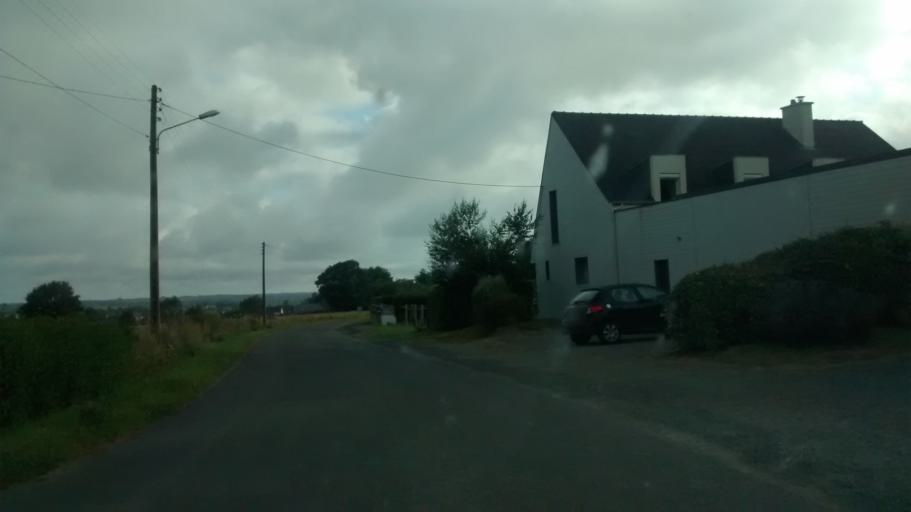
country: FR
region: Brittany
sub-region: Departement d'Ille-et-Vilaine
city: La Gouesniere
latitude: 48.5944
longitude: -1.8984
